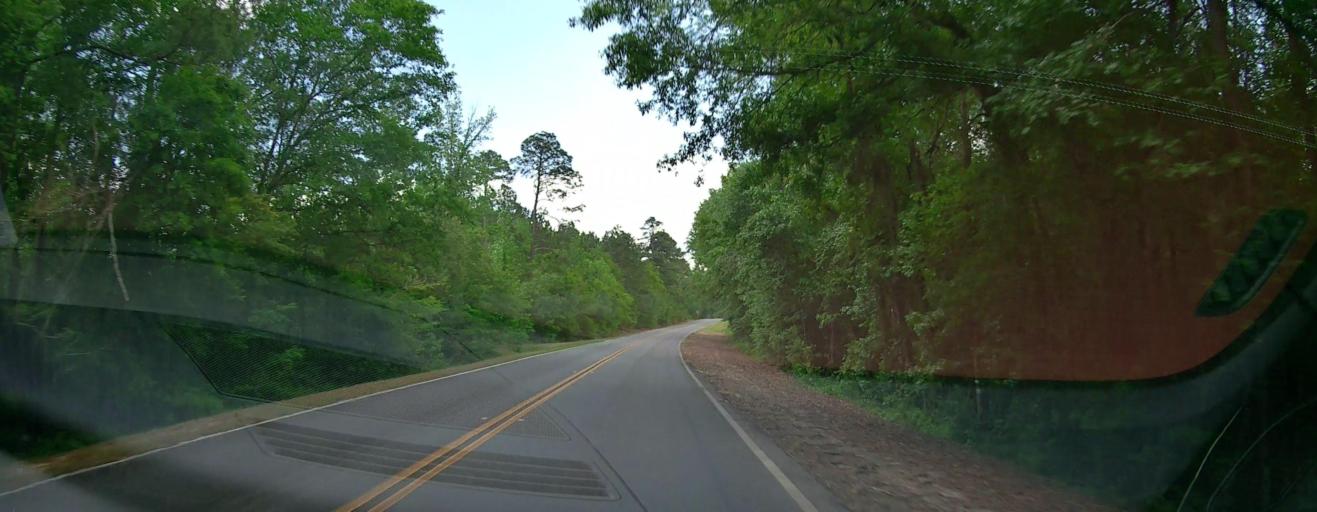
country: US
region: Georgia
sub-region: Treutlen County
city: Soperton
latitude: 32.5203
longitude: -82.6674
